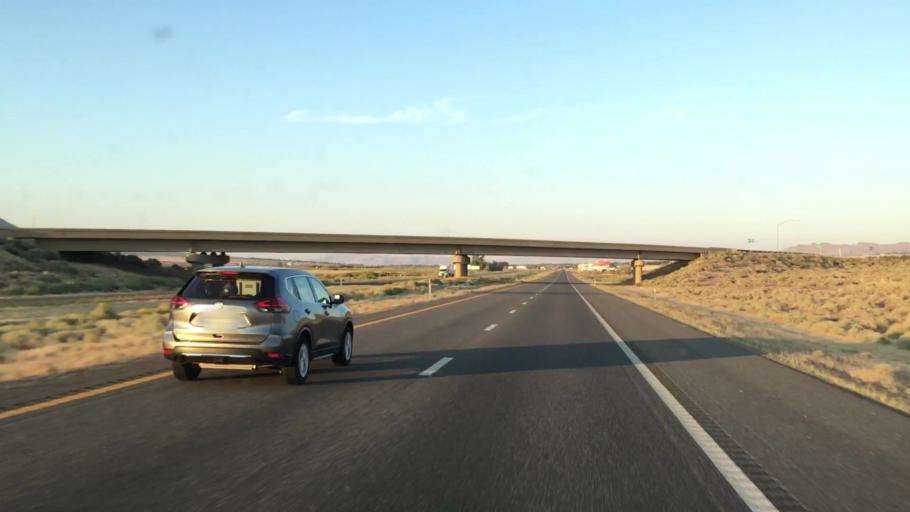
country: US
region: Nevada
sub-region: Humboldt County
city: Winnemucca
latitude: 40.9298
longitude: -117.8050
